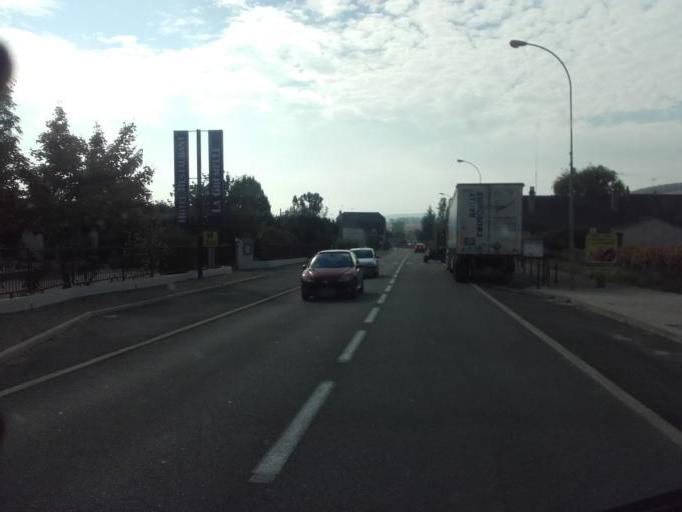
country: FR
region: Bourgogne
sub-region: Departement de la Cote-d'Or
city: Beaune
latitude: 47.0775
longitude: 4.8853
